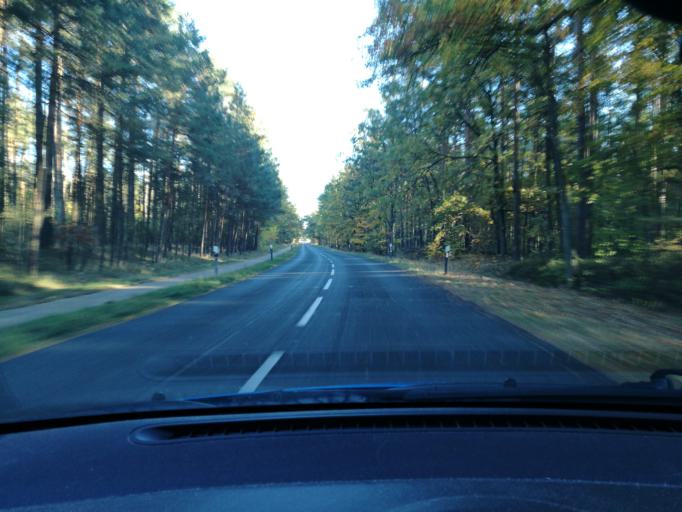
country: DE
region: Lower Saxony
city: Bleckede
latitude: 53.2741
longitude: 10.7780
